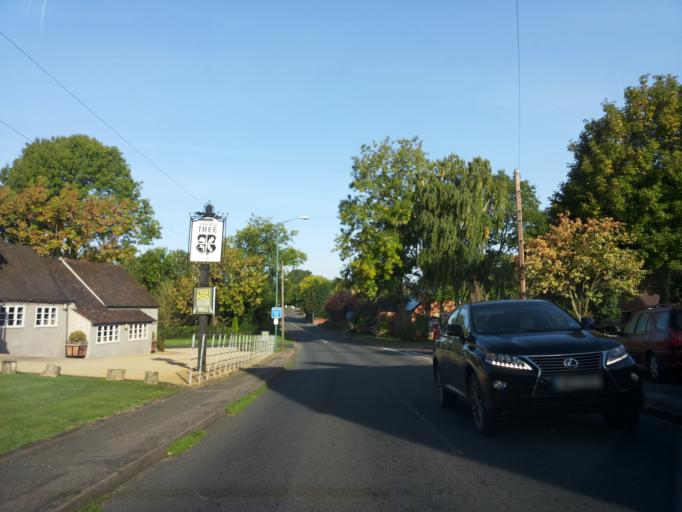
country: GB
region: England
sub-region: Warwickshire
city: Wroxall
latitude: 52.3547
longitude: -1.6970
